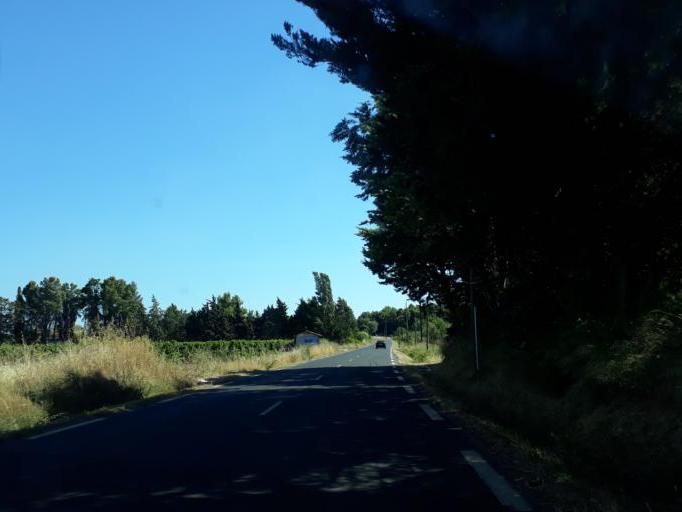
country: FR
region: Languedoc-Roussillon
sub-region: Departement de l'Herault
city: Agde
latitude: 43.3350
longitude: 3.4830
